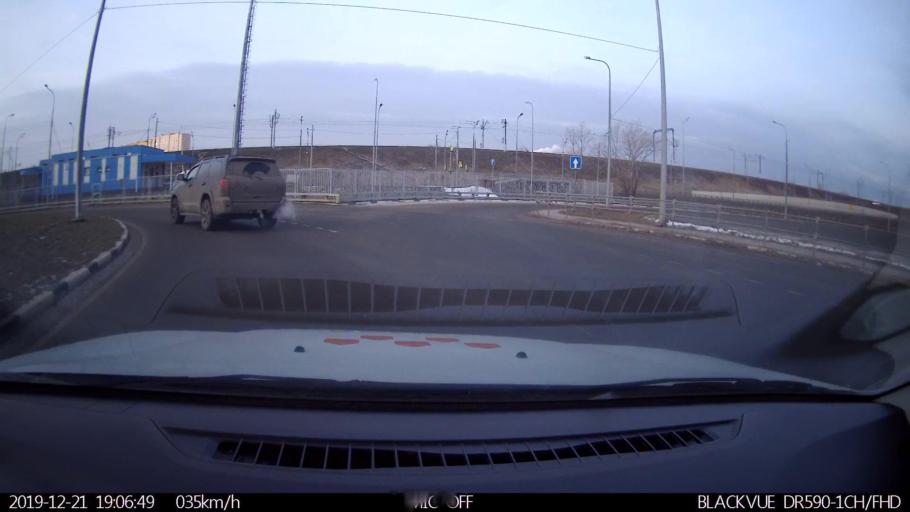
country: RU
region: Nizjnij Novgorod
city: Nizhniy Novgorod
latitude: 56.3432
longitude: 43.9186
